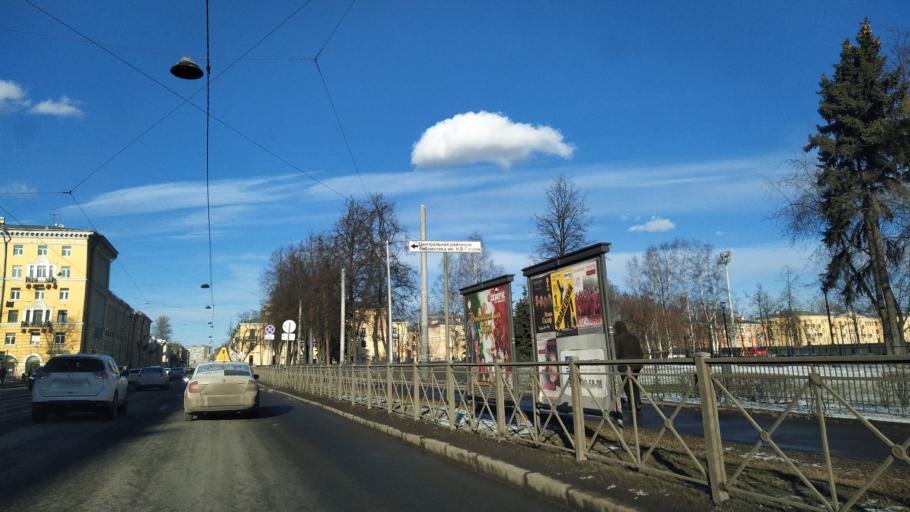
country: RU
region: Leningrad
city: Finlyandskiy
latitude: 59.9472
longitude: 30.4144
